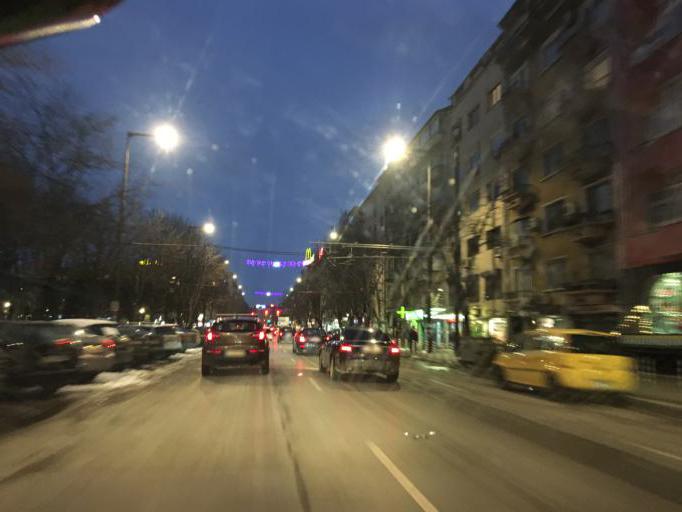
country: BG
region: Sofia-Capital
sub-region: Stolichna Obshtina
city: Sofia
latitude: 42.6888
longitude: 23.3219
